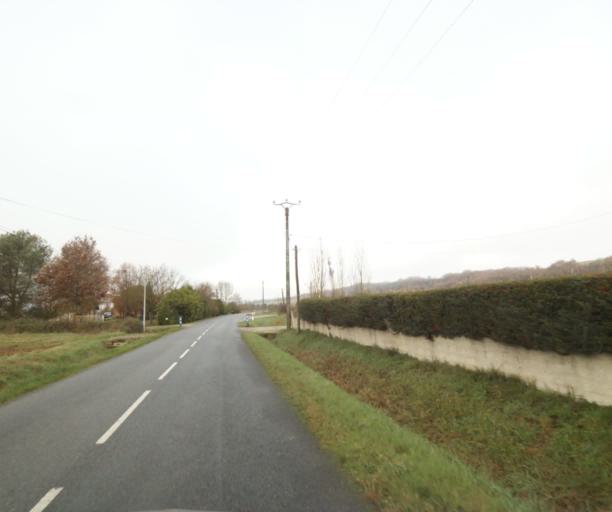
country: FR
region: Midi-Pyrenees
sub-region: Departement de la Haute-Garonne
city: Villemur-sur-Tarn
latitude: 43.8868
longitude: 1.4774
